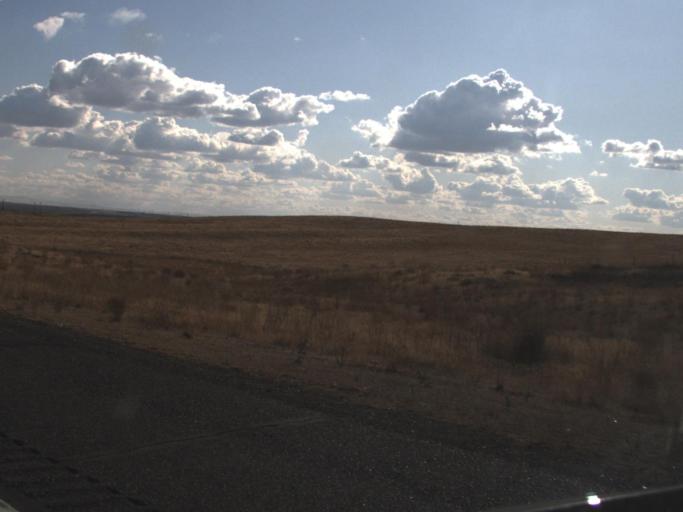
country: US
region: Oregon
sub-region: Umatilla County
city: Umatilla
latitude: 45.9594
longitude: -119.3420
